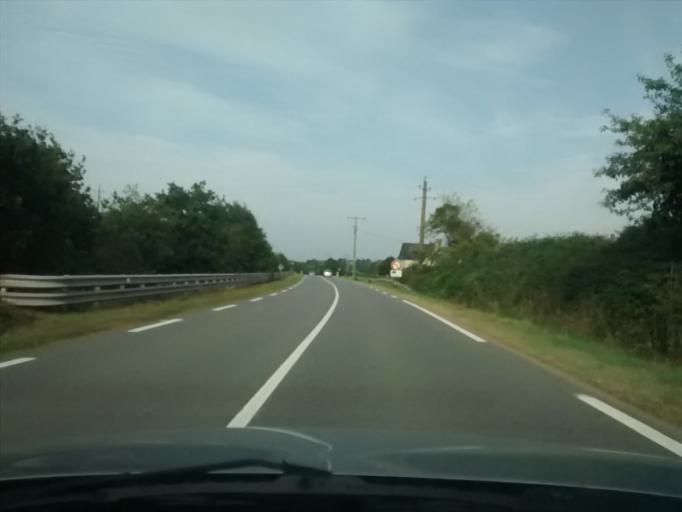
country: FR
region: Brittany
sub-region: Departement d'Ille-et-Vilaine
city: Erbree
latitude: 48.1119
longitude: -1.1277
